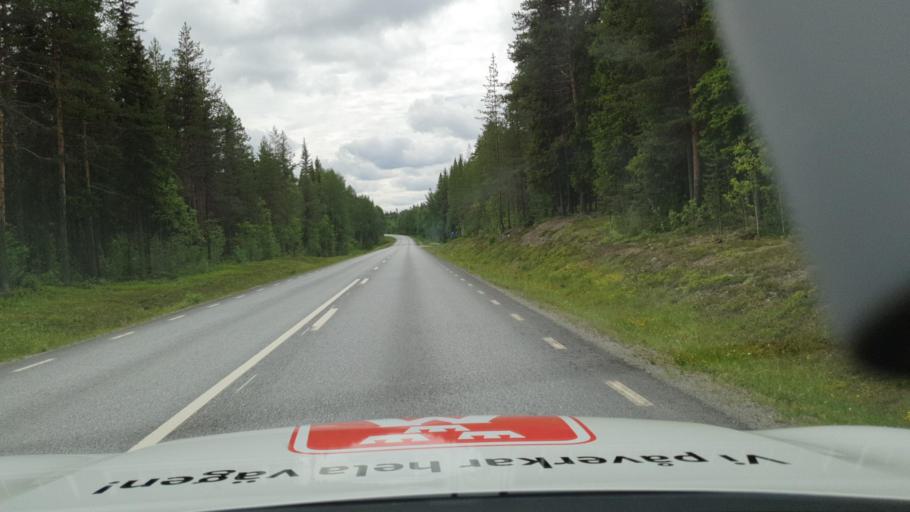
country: SE
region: Vaesterbotten
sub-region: Dorotea Kommun
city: Dorotea
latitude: 64.2418
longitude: 16.3179
